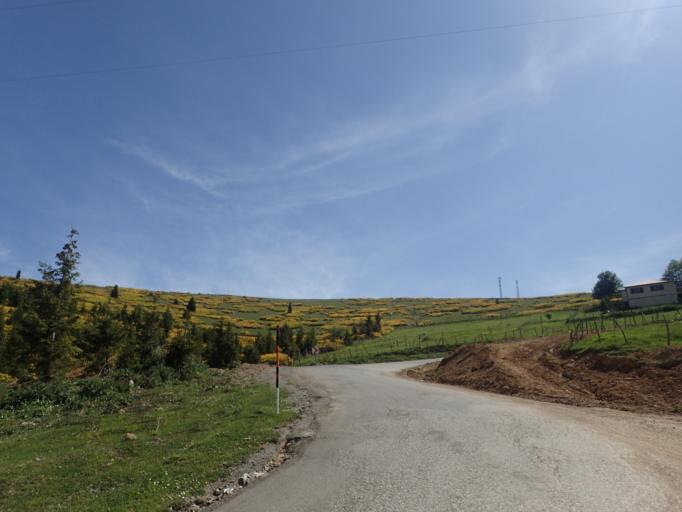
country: TR
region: Ordu
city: Yesilce
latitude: 40.6303
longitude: 37.9547
